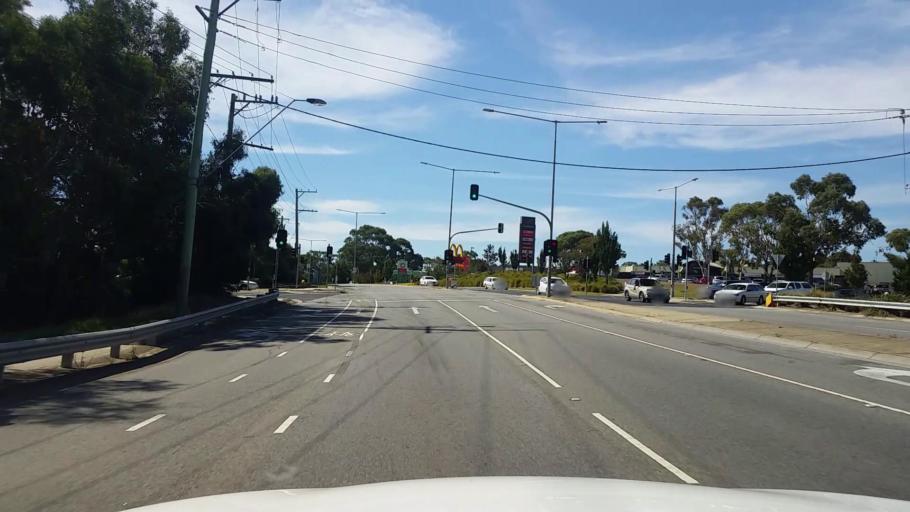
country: AU
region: Victoria
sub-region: Frankston
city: Langwarrin
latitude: -38.1509
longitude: 145.1944
